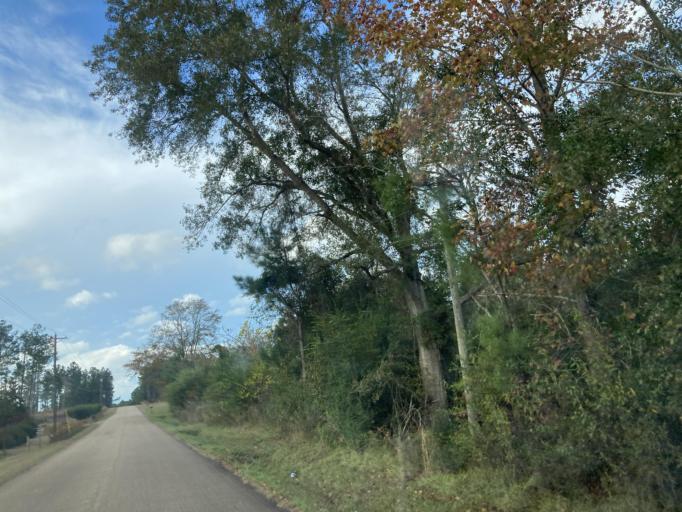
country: US
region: Mississippi
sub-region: Lamar County
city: Purvis
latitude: 31.1349
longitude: -89.6185
